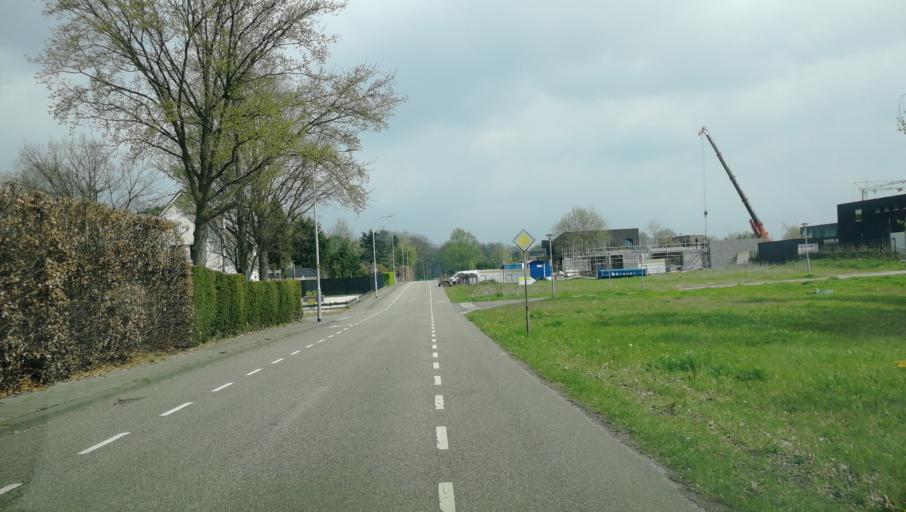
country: NL
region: Limburg
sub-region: Gemeente Venlo
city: Venlo
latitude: 51.3635
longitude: 6.1981
